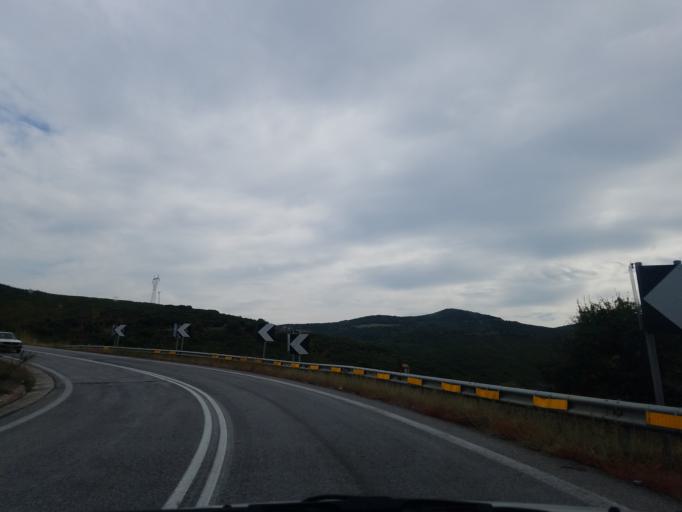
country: GR
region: Central Greece
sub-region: Nomos Fthiotidos
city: Domokos
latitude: 39.1510
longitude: 22.2972
